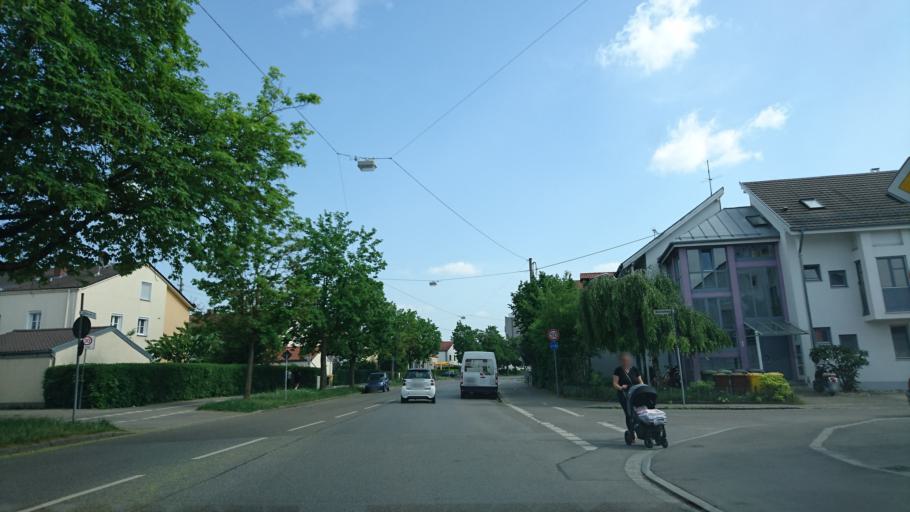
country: DE
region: Bavaria
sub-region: Swabia
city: Augsburg
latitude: 48.3989
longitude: 10.9143
